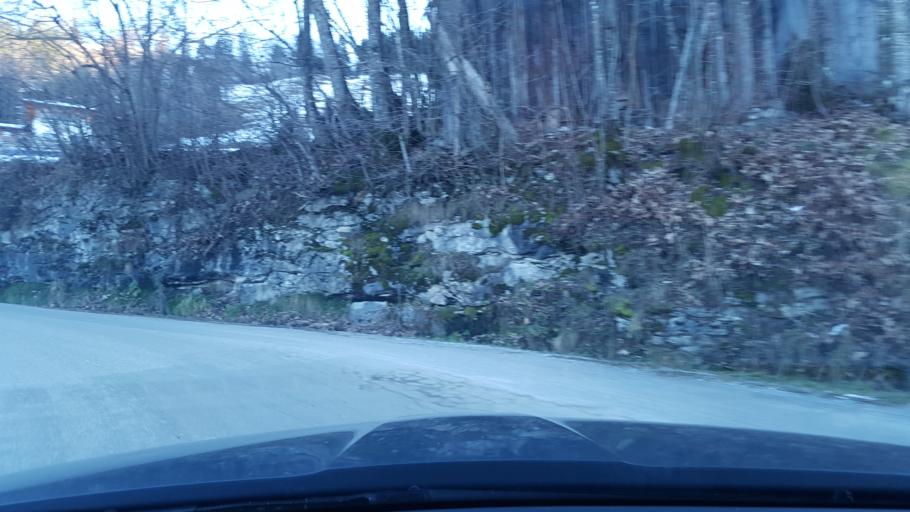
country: AT
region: Salzburg
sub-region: Politischer Bezirk Hallein
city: Scheffau am Tennengebirge
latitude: 47.6444
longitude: 13.2312
